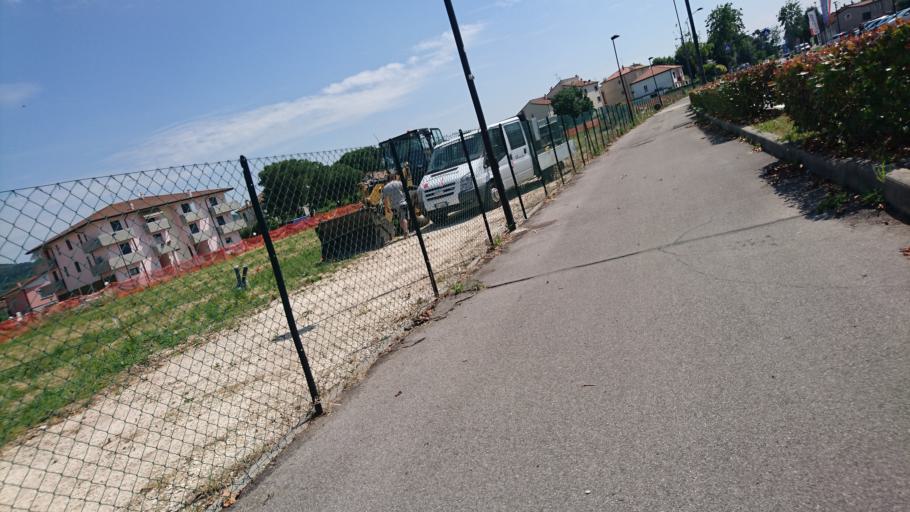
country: IT
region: Veneto
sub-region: Provincia di Padova
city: Este
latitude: 45.2251
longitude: 11.6433
